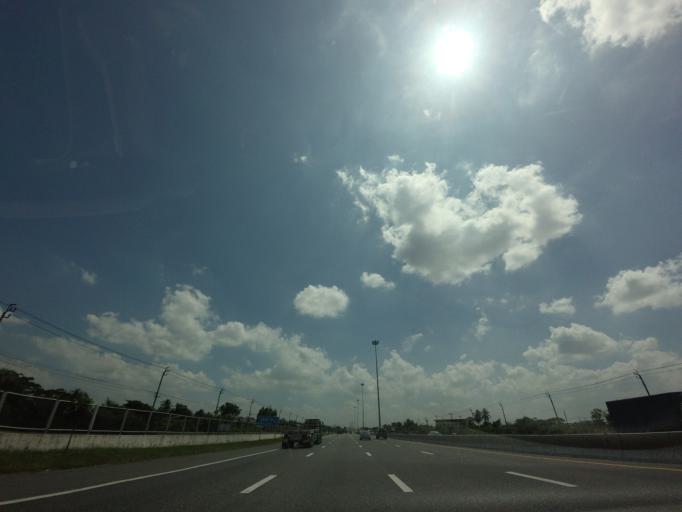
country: TH
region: Bangkok
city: Lat Krabang
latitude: 13.7203
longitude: 100.8152
